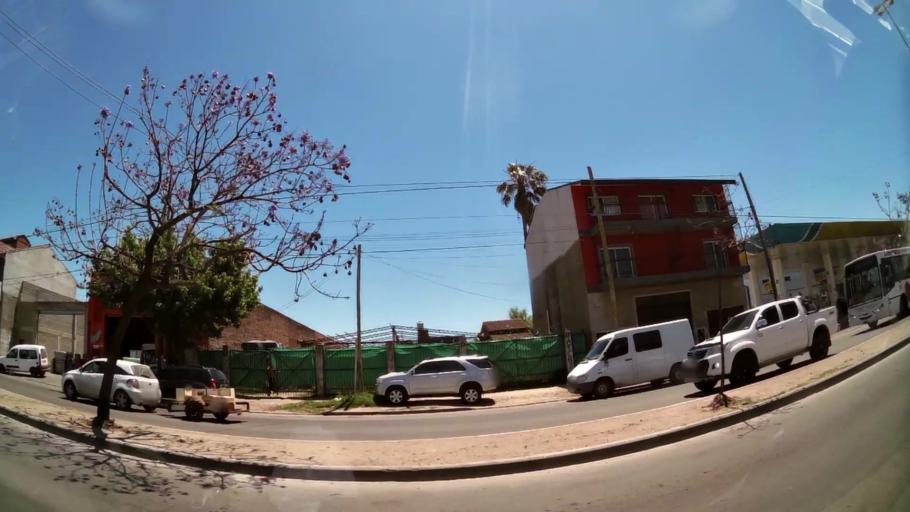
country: AR
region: Buenos Aires
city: Hurlingham
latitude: -34.5028
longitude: -58.7145
